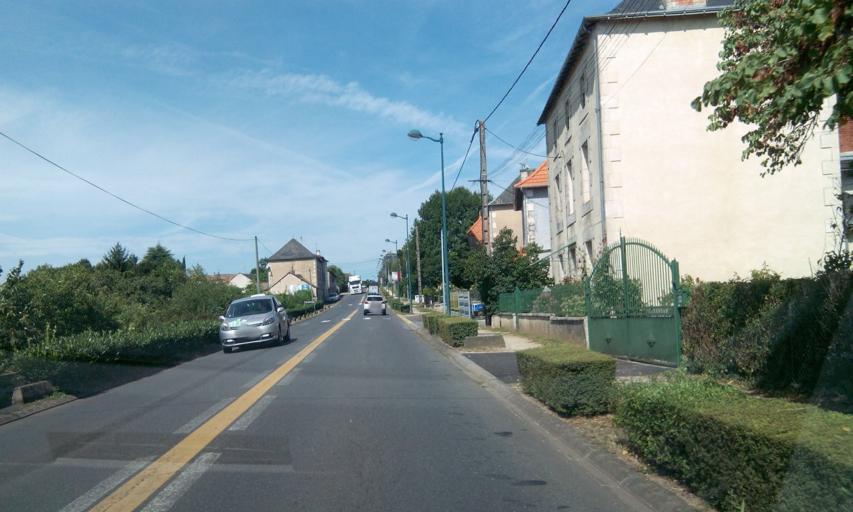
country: FR
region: Poitou-Charentes
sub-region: Departement de la Vienne
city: Savigne
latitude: 46.1591
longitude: 0.3223
